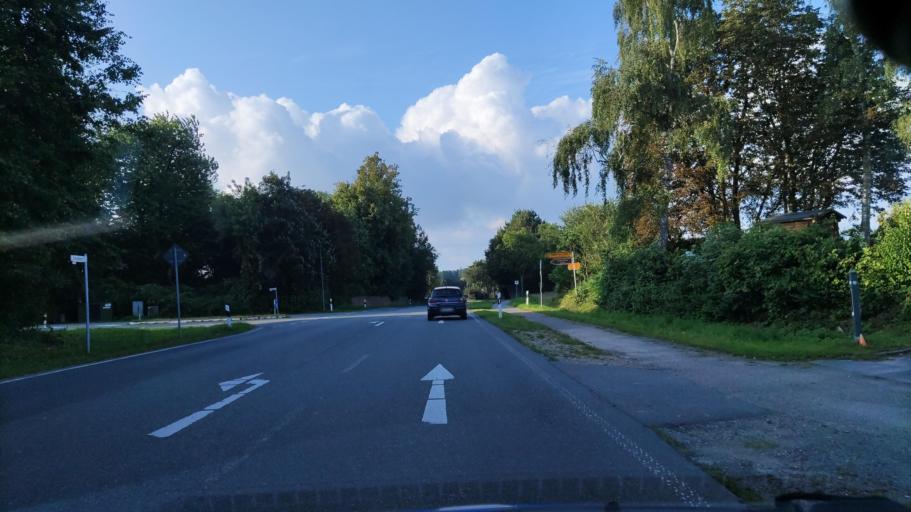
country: DE
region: Schleswig-Holstein
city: Ahrensbok
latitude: 53.9920
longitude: 10.5779
